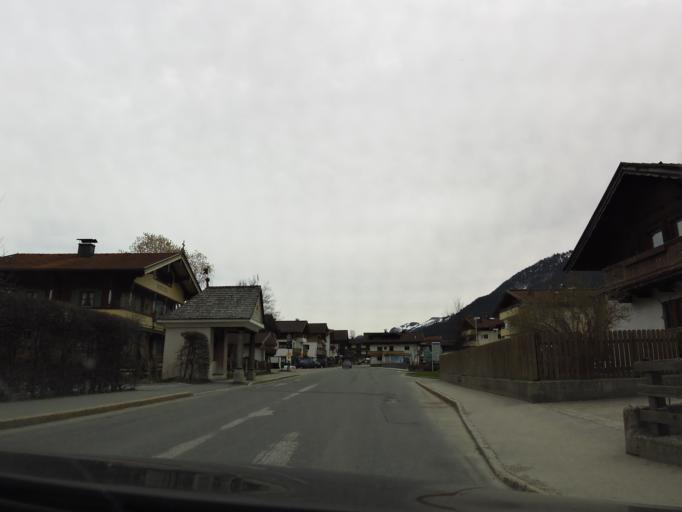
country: AT
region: Tyrol
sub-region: Politischer Bezirk Kitzbuhel
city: Brixen im Thale
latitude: 47.4501
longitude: 12.2532
